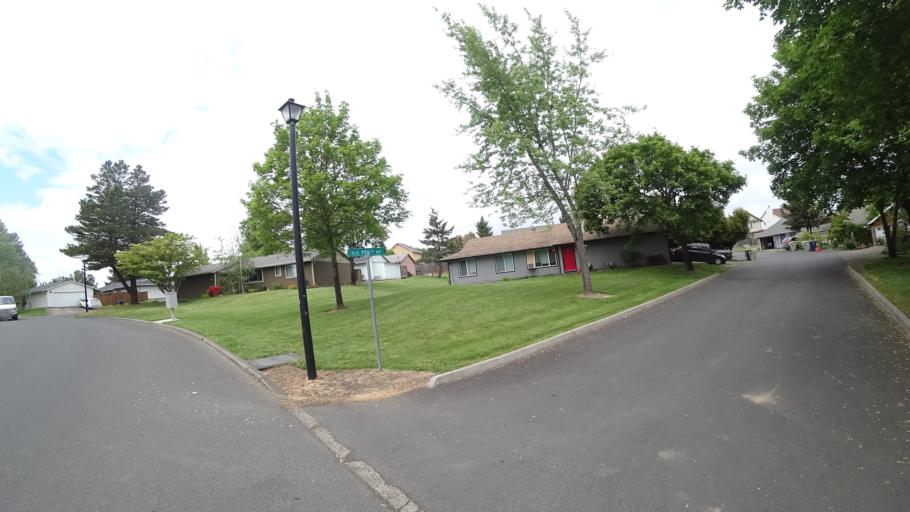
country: US
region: Oregon
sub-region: Washington County
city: Oak Hills
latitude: 45.5221
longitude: -122.8619
